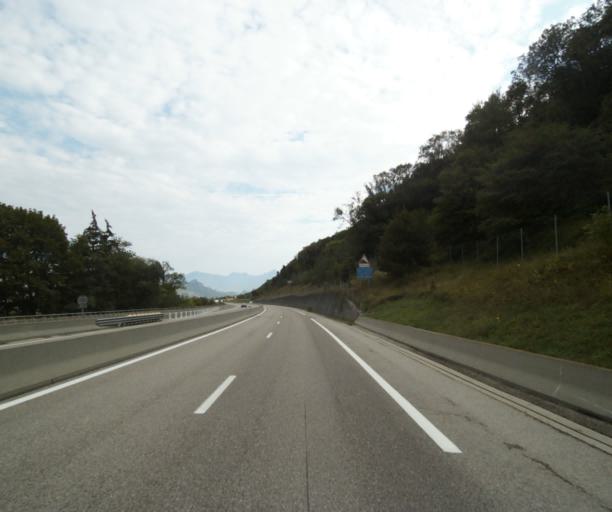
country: FR
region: Rhone-Alpes
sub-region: Departement de l'Isere
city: Le Gua
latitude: 44.9901
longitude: 5.6508
